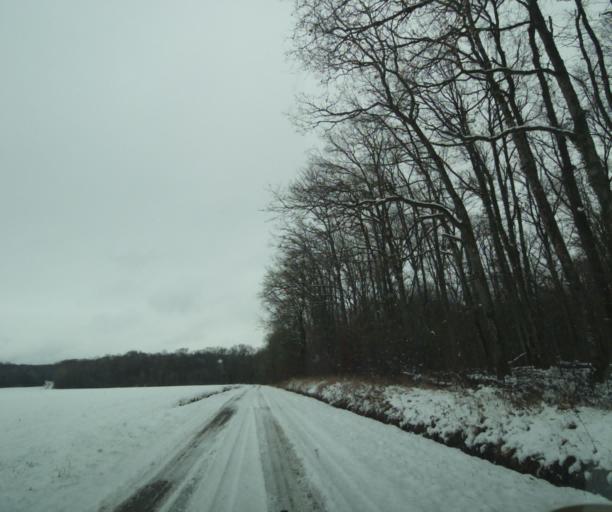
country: FR
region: Champagne-Ardenne
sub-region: Departement de la Haute-Marne
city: Montier-en-Der
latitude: 48.4162
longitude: 4.7525
